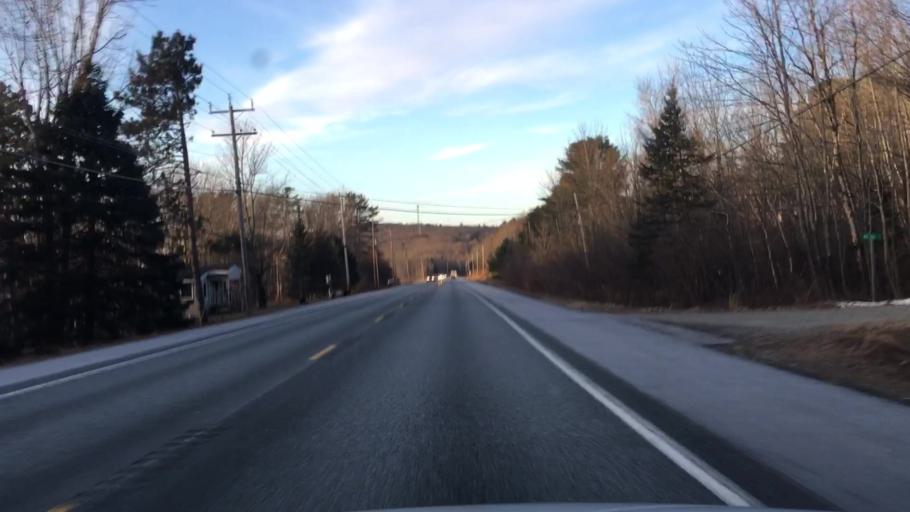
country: US
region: Maine
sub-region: Hancock County
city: Dedham
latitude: 44.7089
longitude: -68.6018
